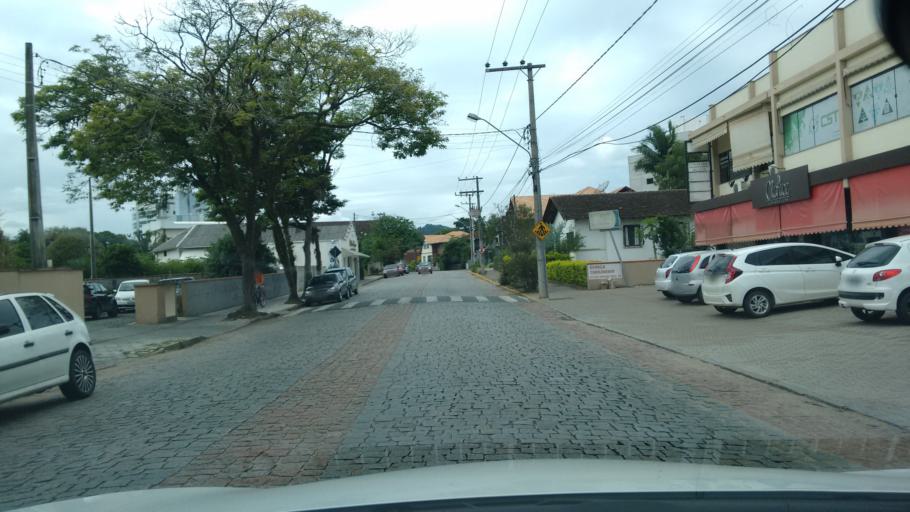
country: BR
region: Santa Catarina
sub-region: Timbo
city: Timbo
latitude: -26.8242
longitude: -49.2709
